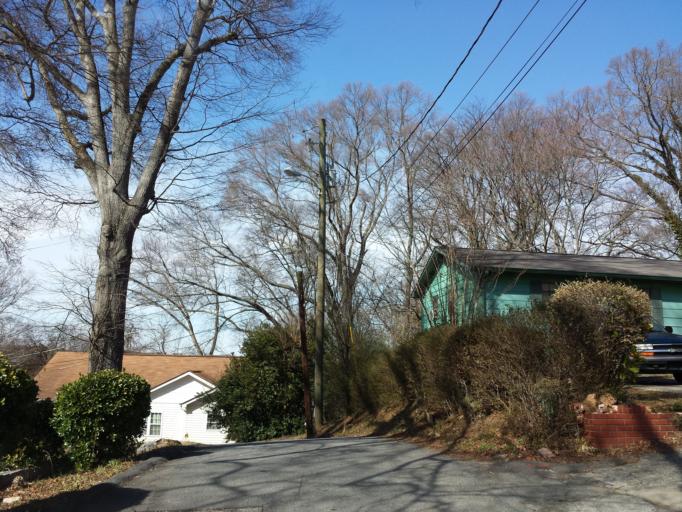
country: US
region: Georgia
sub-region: Cobb County
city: Marietta
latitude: 33.9537
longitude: -84.5400
